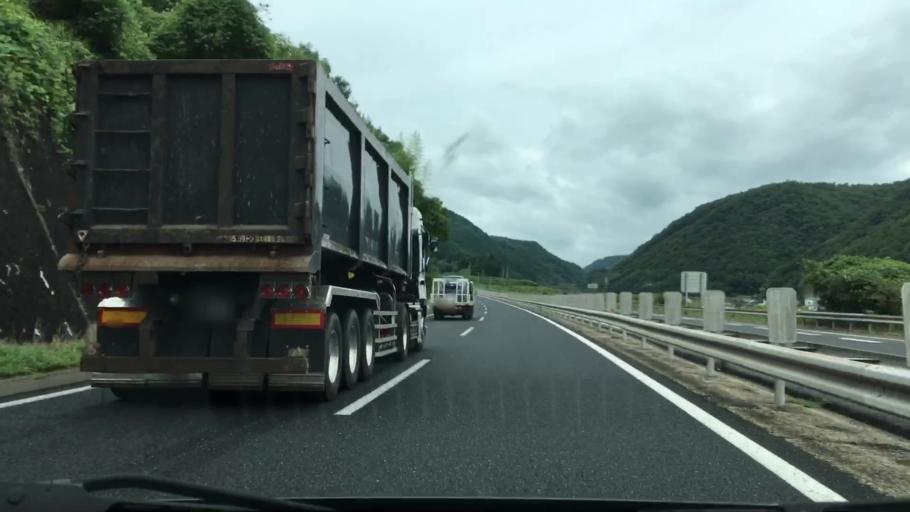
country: JP
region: Hyogo
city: Yamazakicho-nakabirose
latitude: 35.0109
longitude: 134.3036
